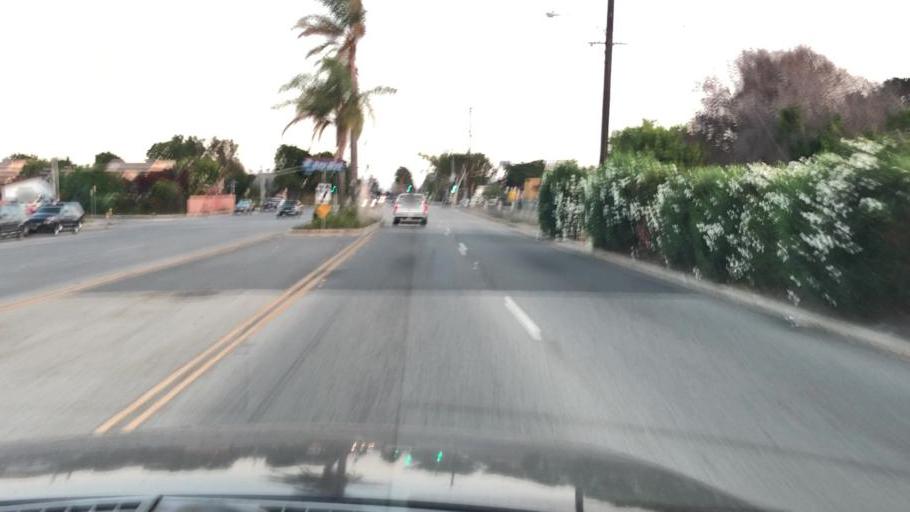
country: US
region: California
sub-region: Ventura County
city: Oxnard
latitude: 34.1796
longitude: -119.1951
